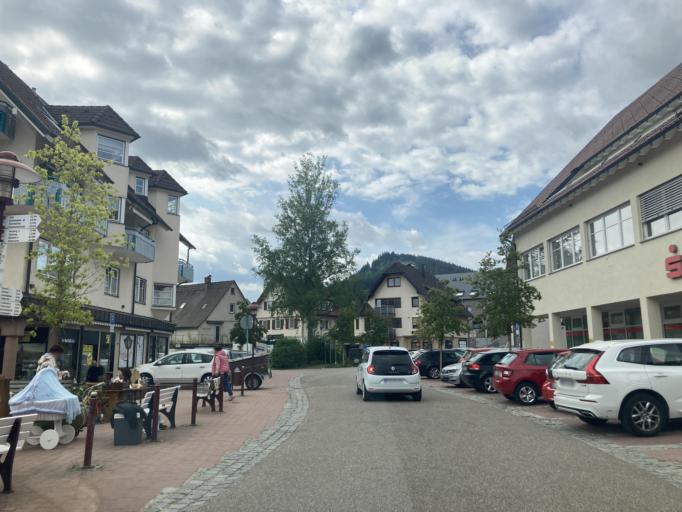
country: DE
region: Baden-Wuerttemberg
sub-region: Karlsruhe Region
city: Baiersbronn
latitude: 48.5081
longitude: 8.3692
